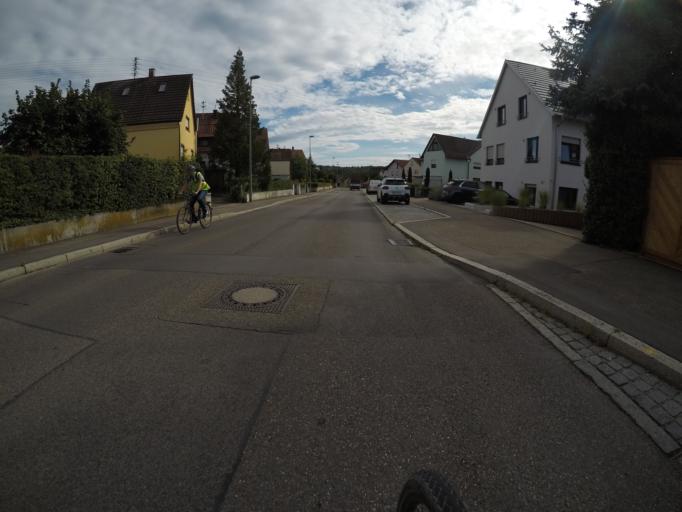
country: DE
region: Baden-Wuerttemberg
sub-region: Regierungsbezirk Stuttgart
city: Freiberg am Neckar
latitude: 48.9160
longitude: 9.2188
